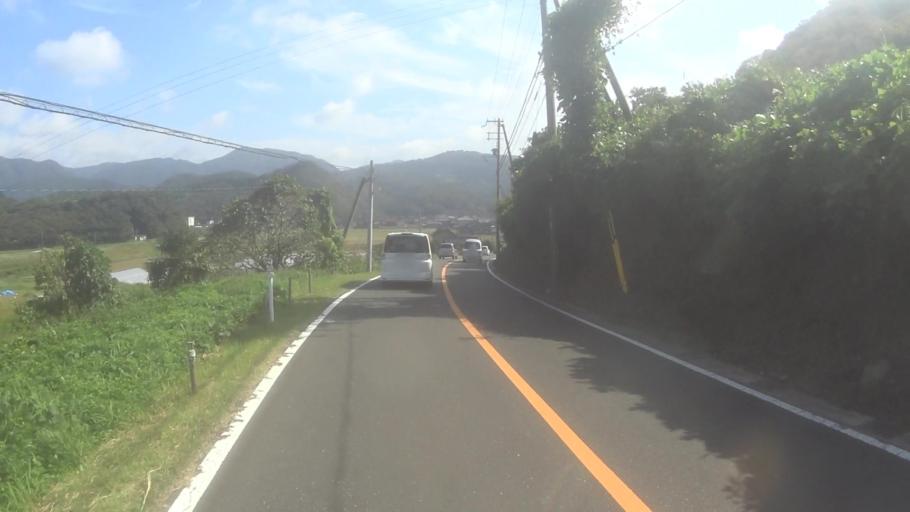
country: JP
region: Kyoto
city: Miyazu
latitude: 35.7512
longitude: 135.1589
